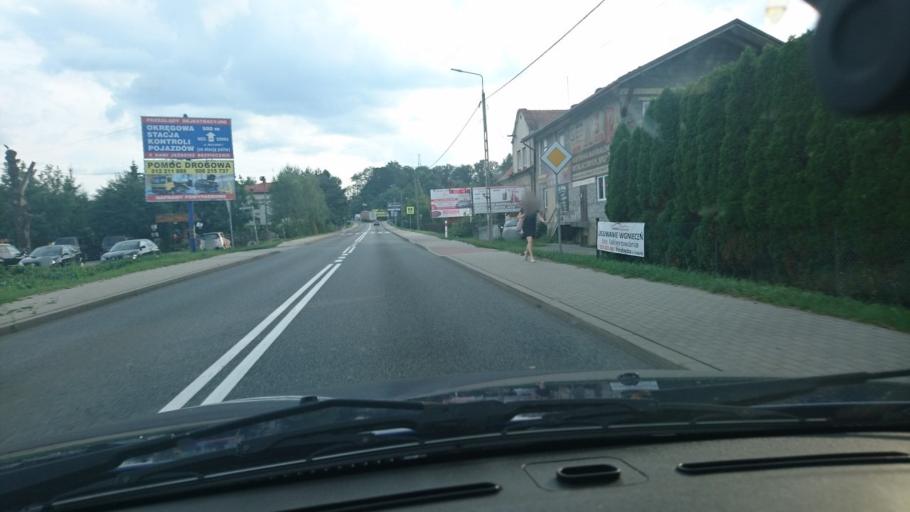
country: PL
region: Silesian Voivodeship
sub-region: Powiat zywiecki
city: Wegierska Gorka
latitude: 49.6116
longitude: 19.1182
